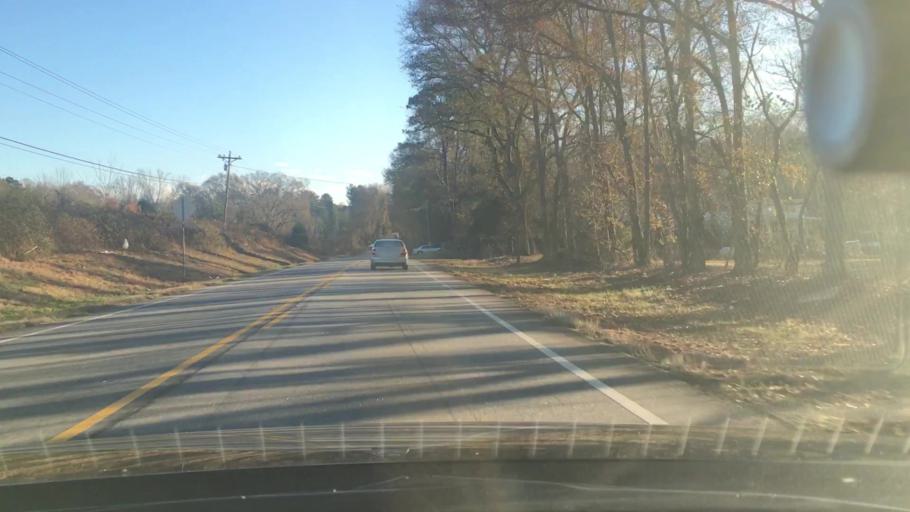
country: US
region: Georgia
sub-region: Spalding County
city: Experiment
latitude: 33.2393
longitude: -84.4008
